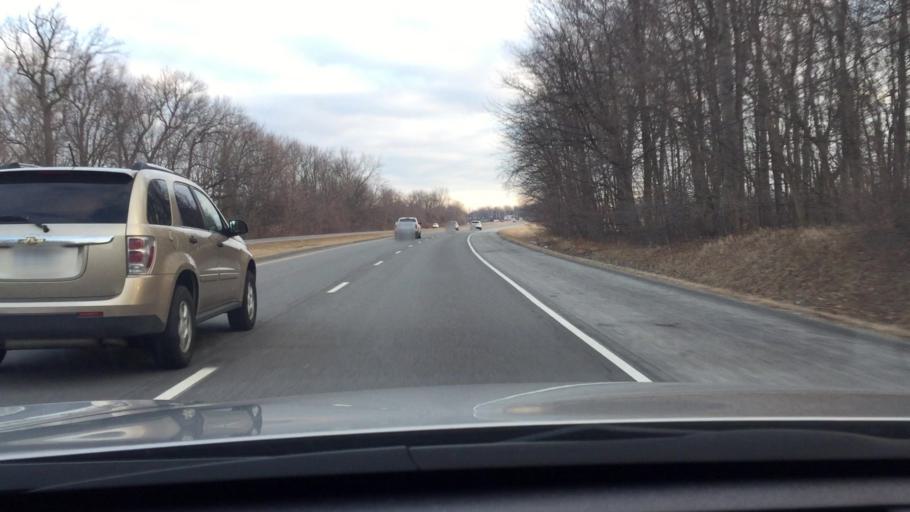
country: US
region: Indiana
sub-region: Hamilton County
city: Noblesville
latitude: 40.0145
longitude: -86.0023
